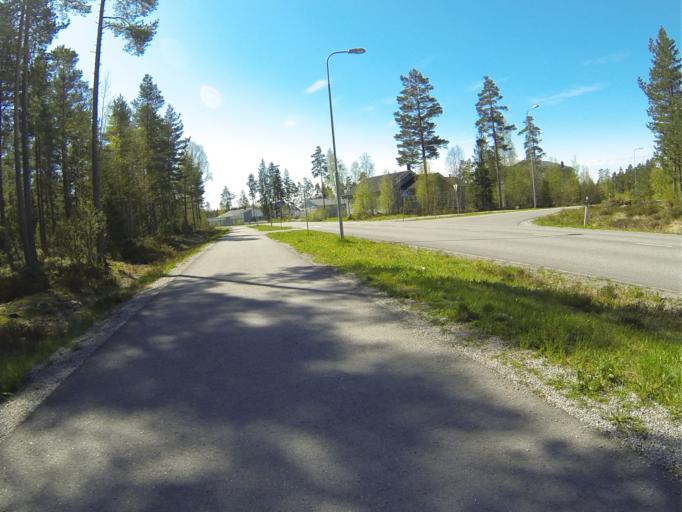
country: FI
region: Varsinais-Suomi
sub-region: Salo
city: Salo
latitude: 60.4001
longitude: 23.1914
